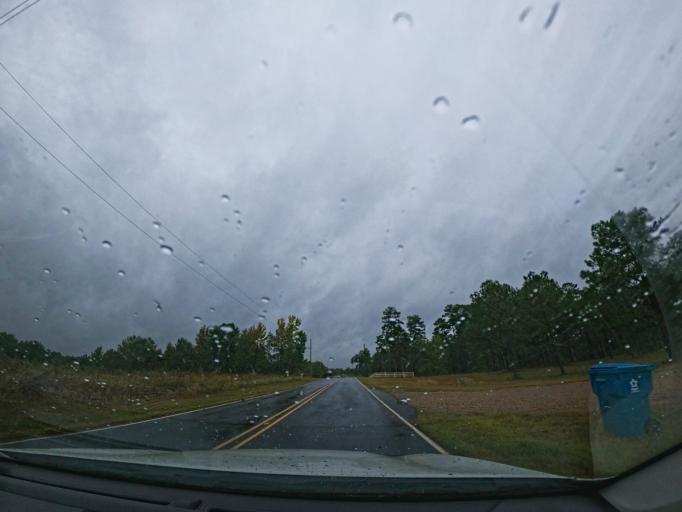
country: US
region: Louisiana
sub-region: Webster Parish
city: Minden
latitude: 32.6472
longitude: -93.2687
